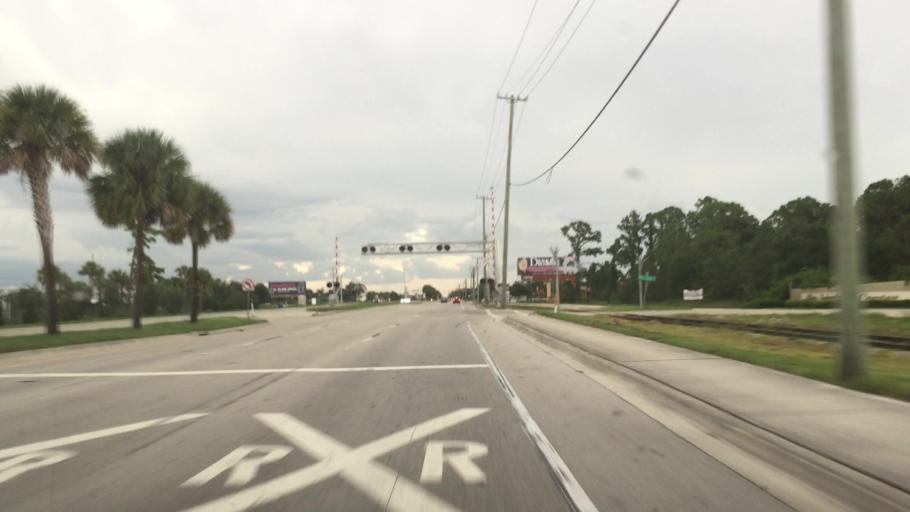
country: US
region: Florida
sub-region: Lee County
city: San Carlos Park
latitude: 26.4926
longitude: -81.8316
